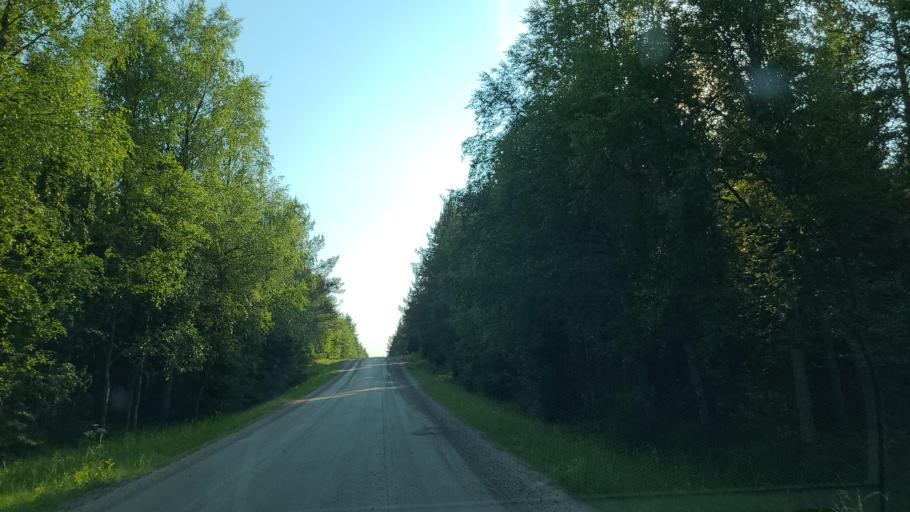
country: SE
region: Vaesterbotten
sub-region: Skelleftea Kommun
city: Burea
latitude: 64.3627
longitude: 21.4426
